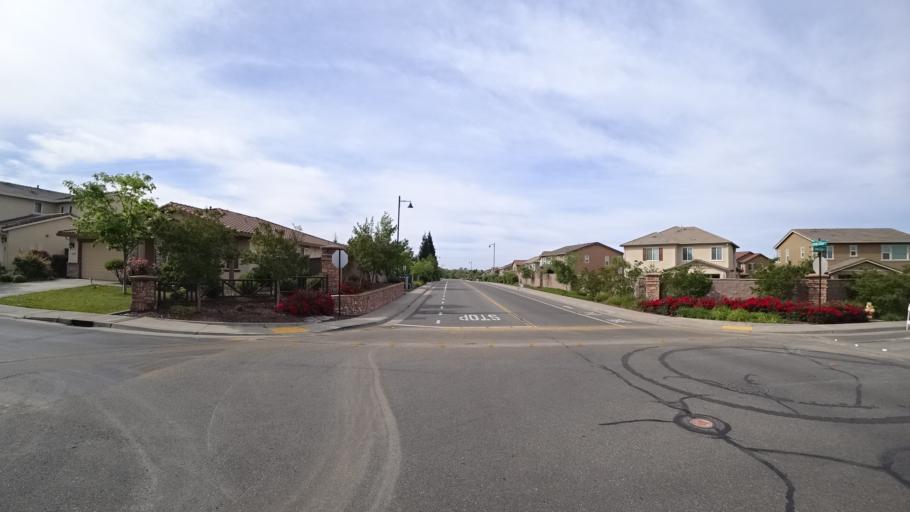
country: US
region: California
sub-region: Placer County
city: Lincoln
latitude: 38.8371
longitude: -121.2802
